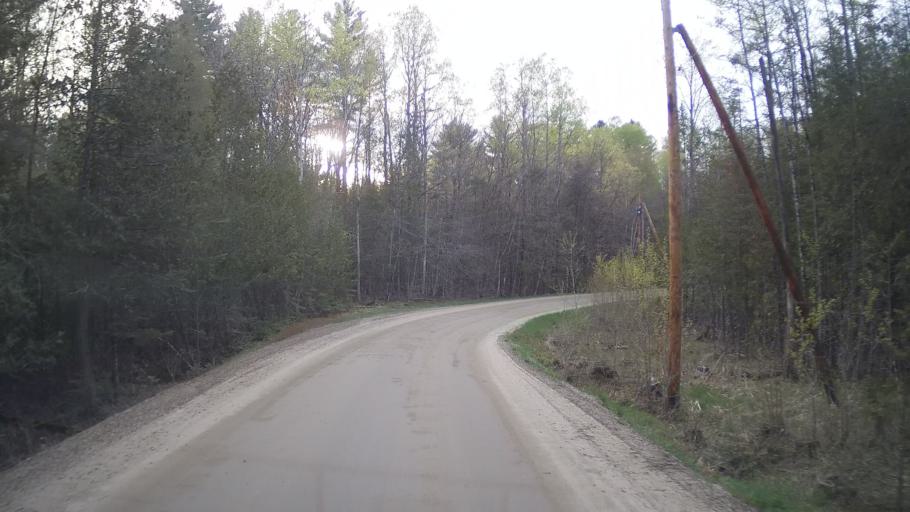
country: US
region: Vermont
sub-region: Caledonia County
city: Lyndonville
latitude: 44.5942
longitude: -71.9579
